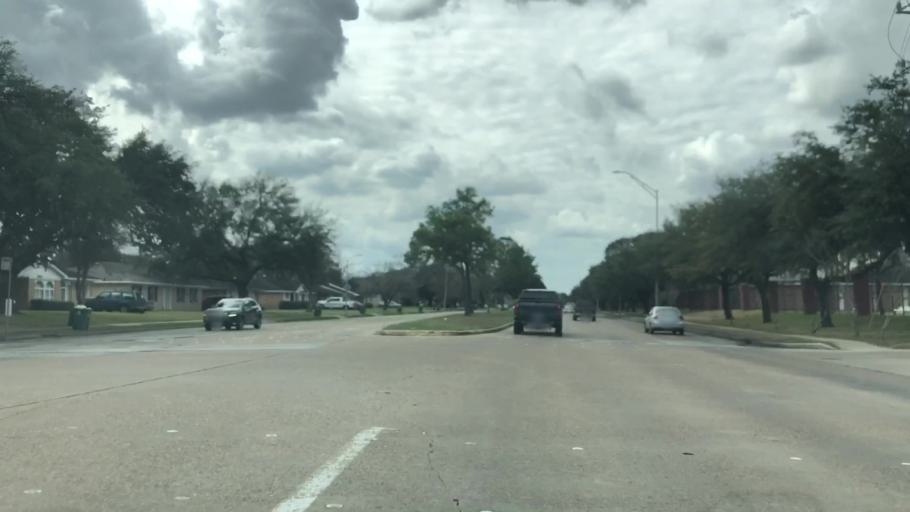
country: US
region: Texas
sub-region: Harris County
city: Bellaire
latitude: 29.6912
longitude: -95.5137
